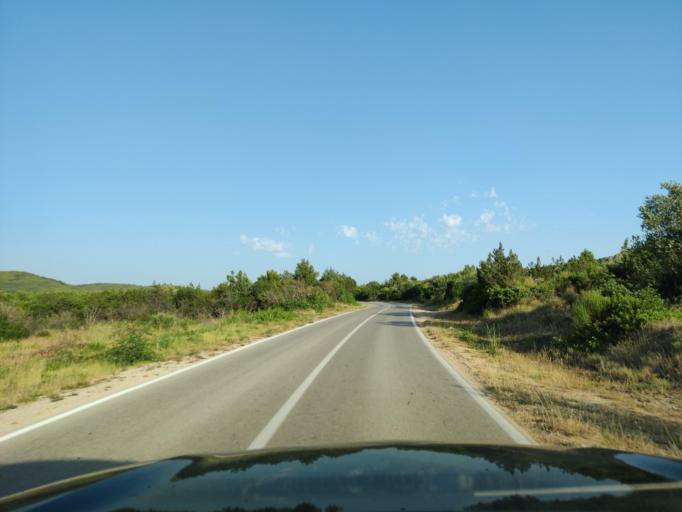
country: HR
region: Sibensko-Kniniska
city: Tribunj
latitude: 43.7852
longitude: 15.7076
